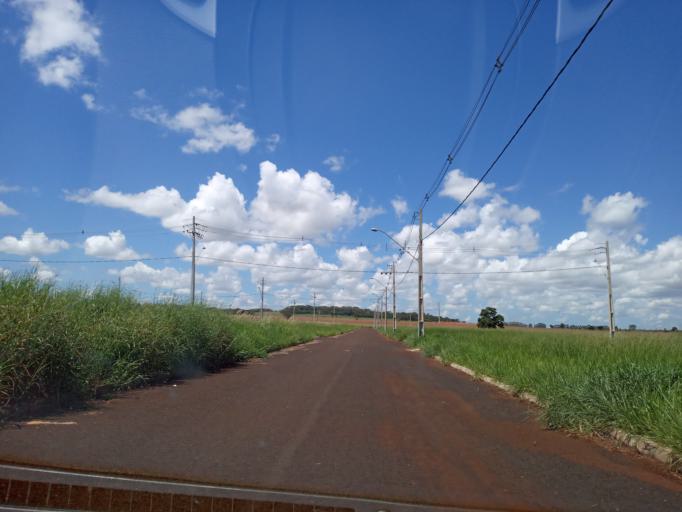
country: BR
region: Minas Gerais
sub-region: Centralina
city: Centralina
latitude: -18.5966
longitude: -49.1995
